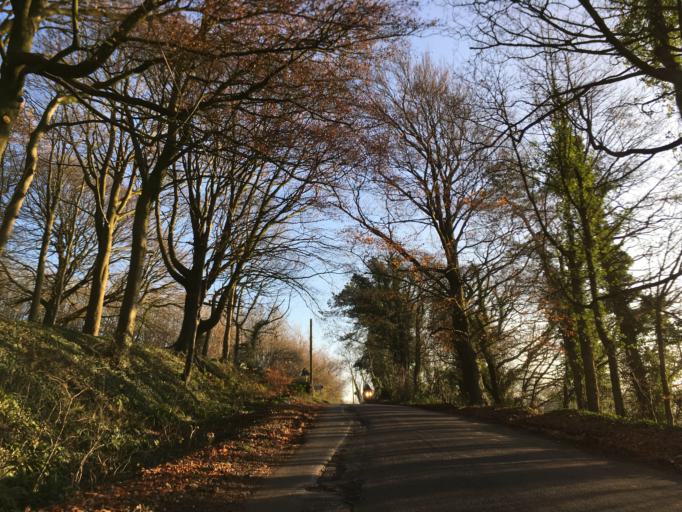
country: GB
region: England
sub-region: South Gloucestershire
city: Horton
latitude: 51.5550
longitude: -2.3394
